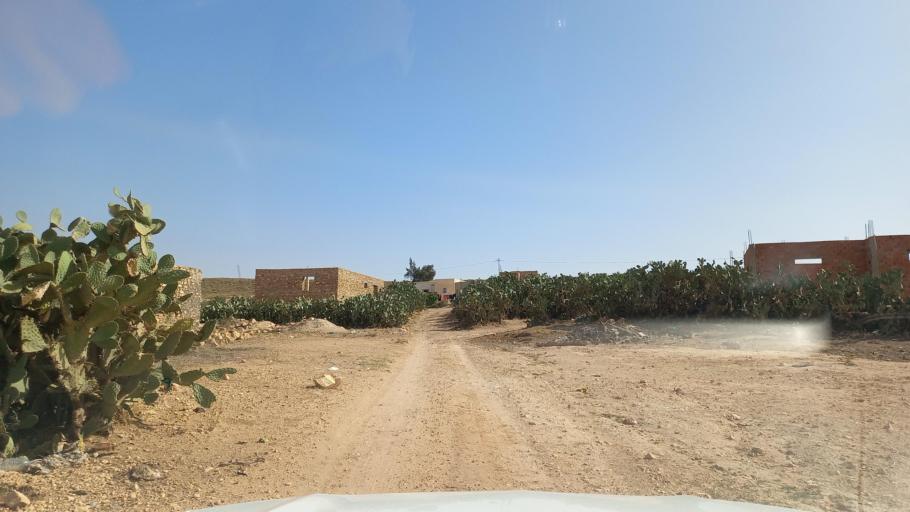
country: TN
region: Al Qasrayn
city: Kasserine
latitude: 35.2072
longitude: 8.9784
